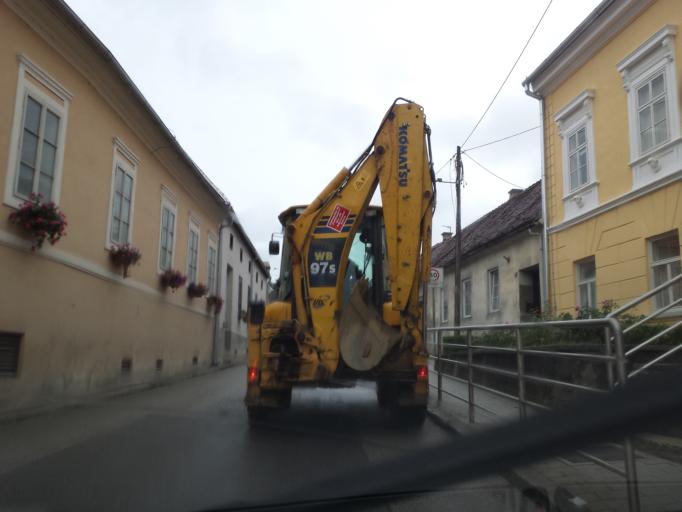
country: HR
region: Zagrebacka
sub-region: Grad Samobor
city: Samobor
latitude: 45.8027
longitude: 15.7087
